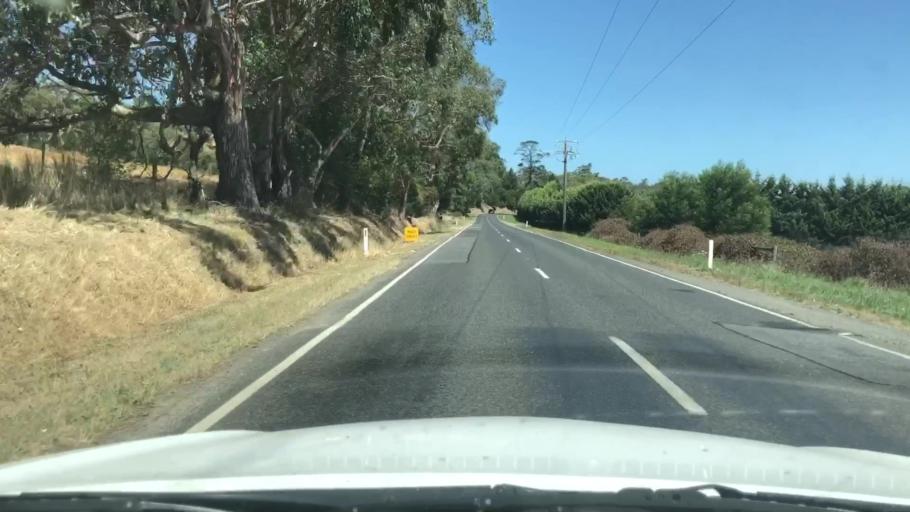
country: AU
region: Victoria
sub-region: Yarra Ranges
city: Woori Yallock
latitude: -37.7964
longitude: 145.5239
